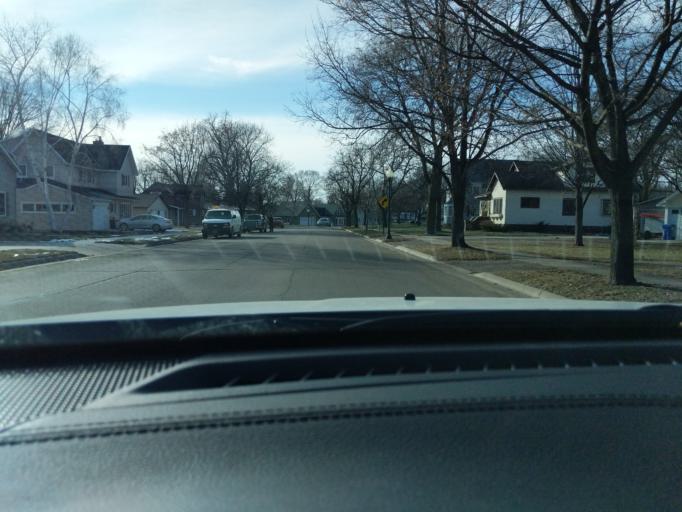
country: US
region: Minnesota
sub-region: Yellow Medicine County
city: Granite Falls
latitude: 44.8074
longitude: -95.5421
